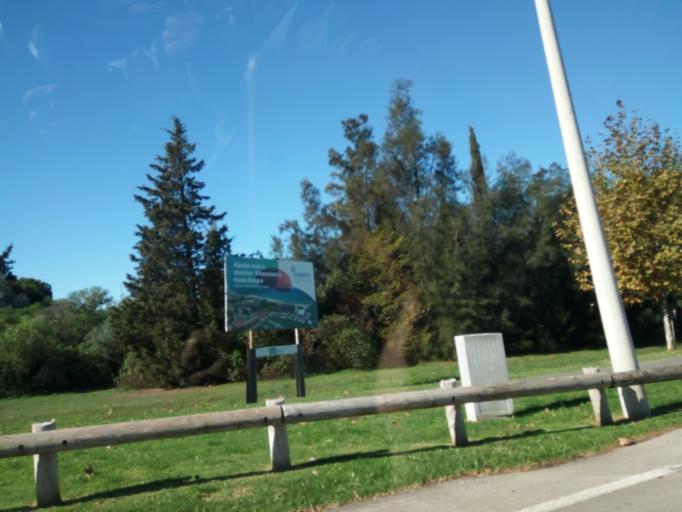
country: PT
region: Faro
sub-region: Loule
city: Vilamoura
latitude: 37.1025
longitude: -8.1245
